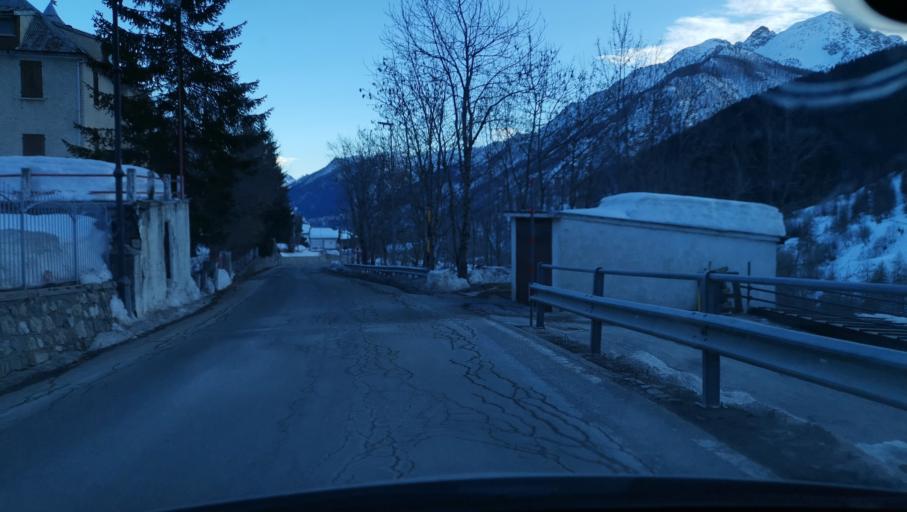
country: IT
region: Piedmont
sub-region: Provincia di Cuneo
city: Bersezio
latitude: 44.3782
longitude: 6.9699
